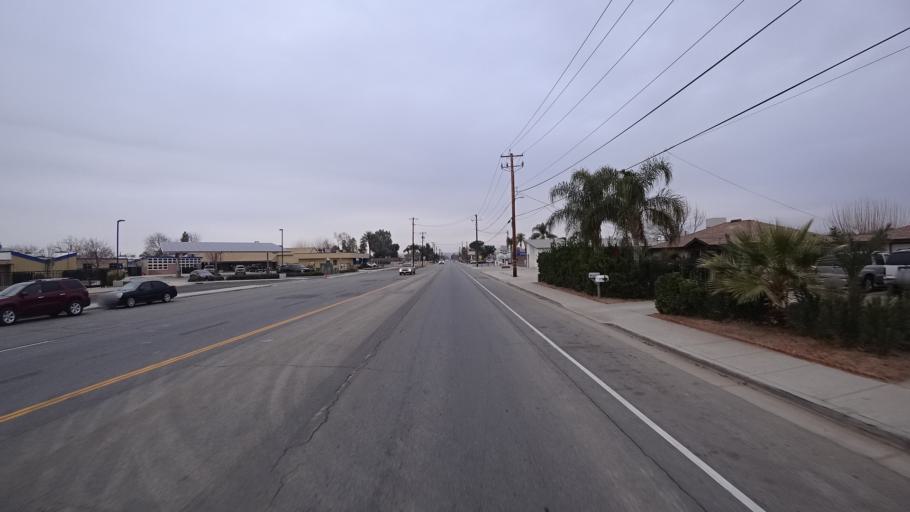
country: US
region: California
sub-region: Kern County
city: Lamont
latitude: 35.3405
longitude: -118.9320
